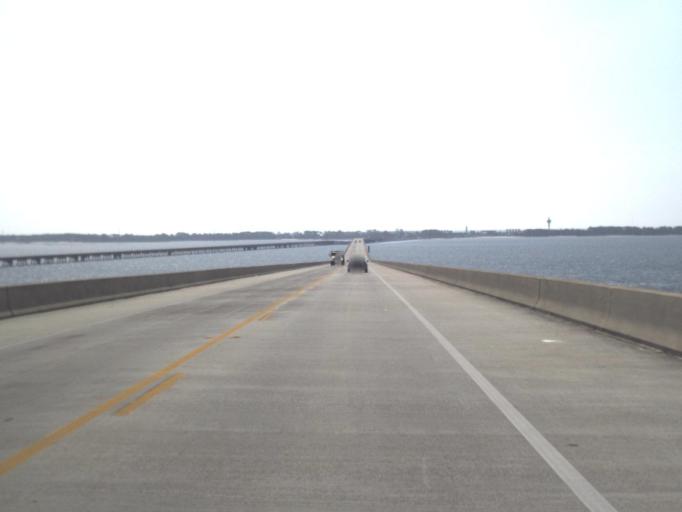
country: US
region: Florida
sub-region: Franklin County
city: Eastpoint
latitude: 29.6818
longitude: -84.8783
